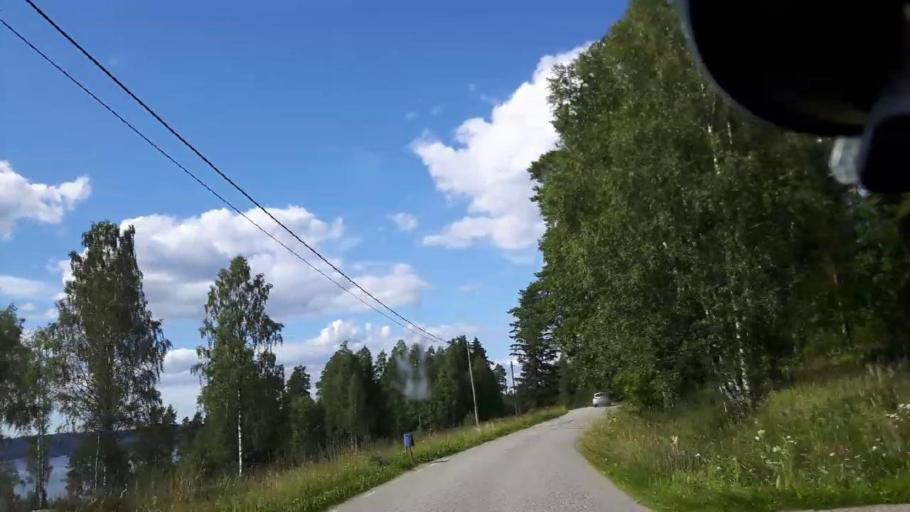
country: SE
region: Jaemtland
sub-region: Braecke Kommun
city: Braecke
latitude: 62.8826
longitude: 15.2736
